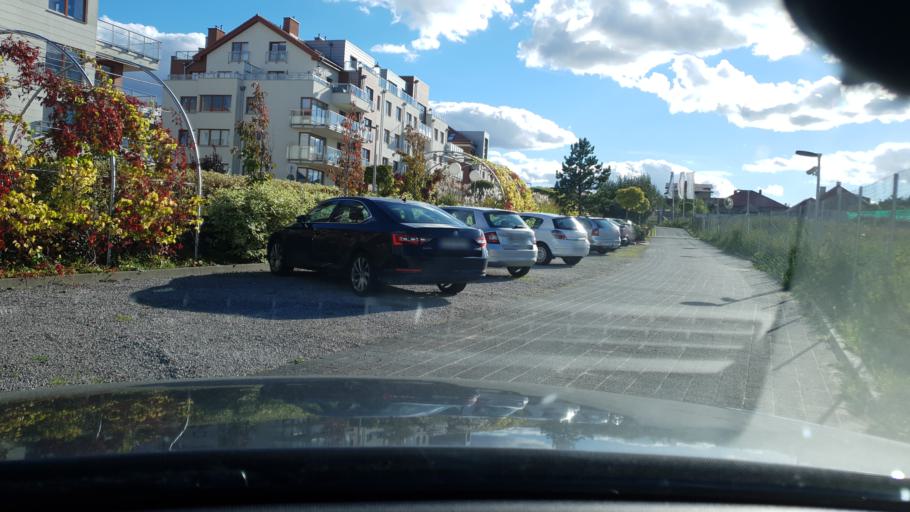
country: PL
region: Pomeranian Voivodeship
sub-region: Powiat kartuski
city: Chwaszczyno
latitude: 54.5012
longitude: 18.4371
